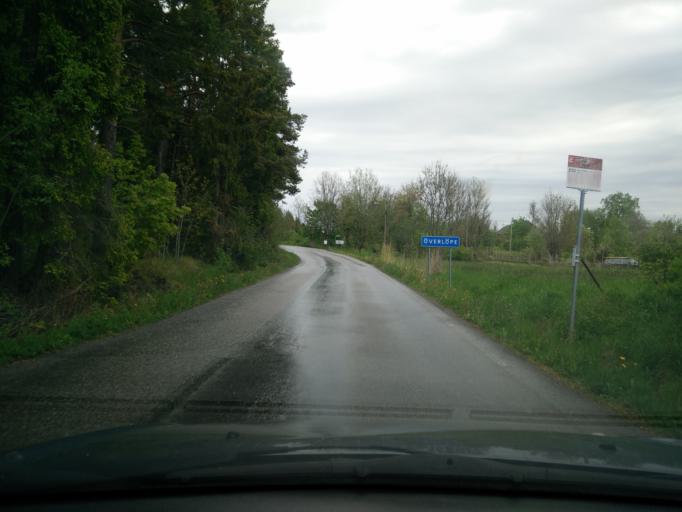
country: SE
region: Stockholm
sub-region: Norrtalje Kommun
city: Bjorko
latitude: 59.8255
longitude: 18.9078
